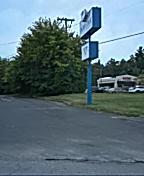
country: US
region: Kentucky
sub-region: Jefferson County
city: Middletown
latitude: 38.2487
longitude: -85.5325
